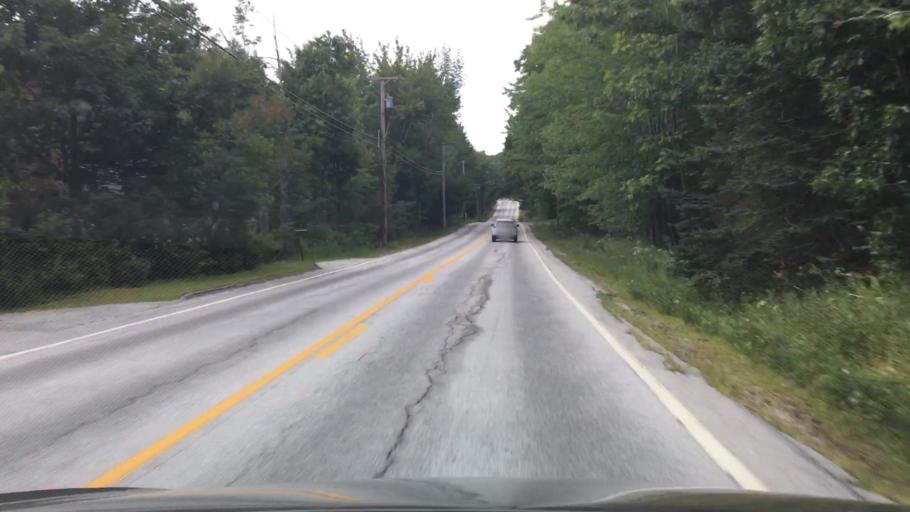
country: US
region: Maine
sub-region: Hancock County
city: Penobscot
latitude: 44.4326
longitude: -68.6058
